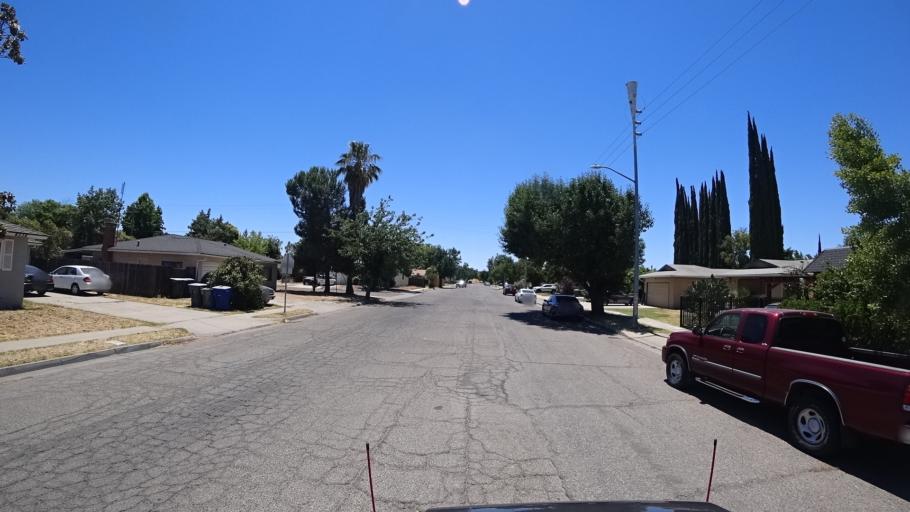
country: US
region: California
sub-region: Fresno County
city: Tarpey Village
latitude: 36.8003
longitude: -119.7452
